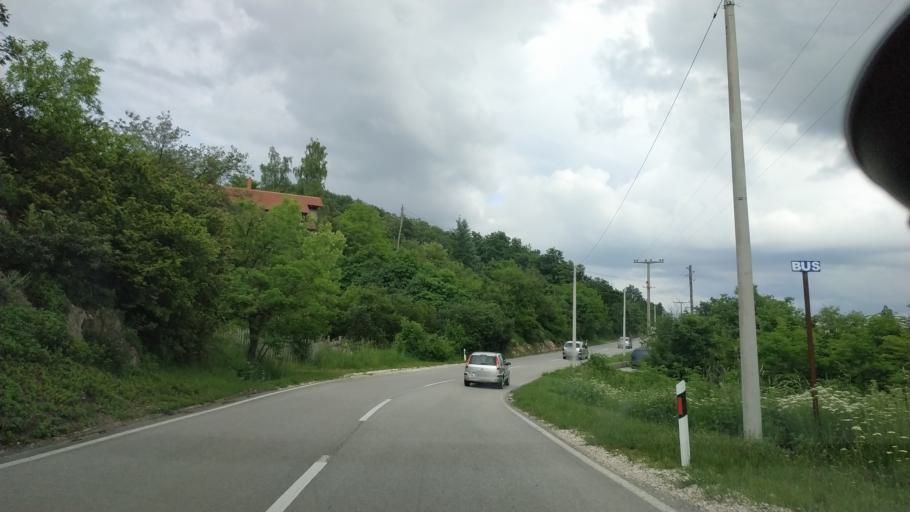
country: RS
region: Central Serbia
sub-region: Borski Okrug
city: Bor
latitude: 44.0507
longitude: 22.0736
